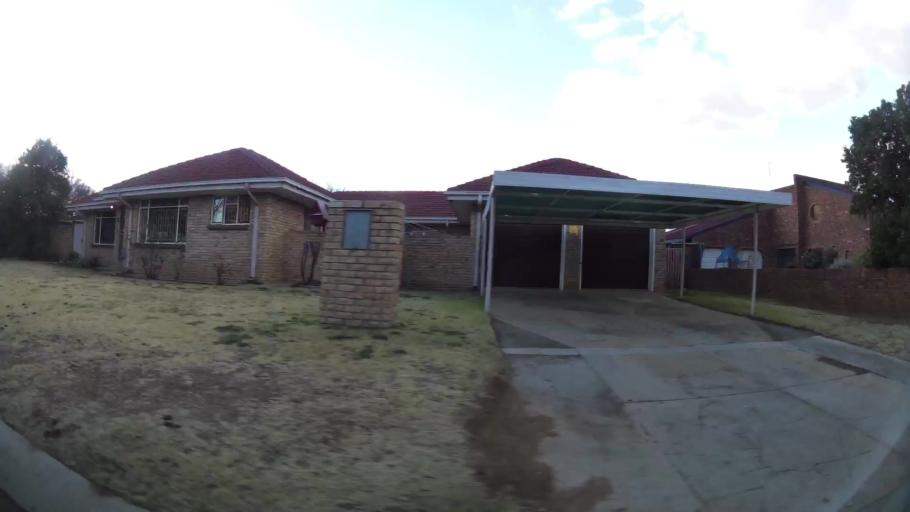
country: ZA
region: North-West
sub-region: Dr Kenneth Kaunda District Municipality
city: Potchefstroom
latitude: -26.7389
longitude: 27.0985
